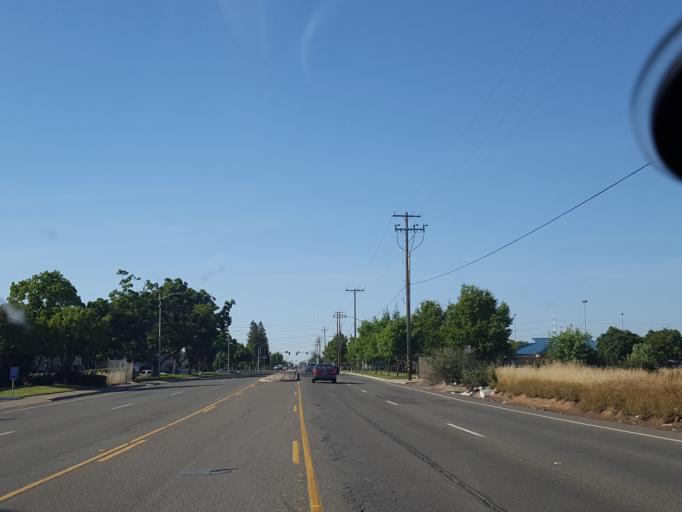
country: US
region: California
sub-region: Sacramento County
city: Florin
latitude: 38.5028
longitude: -121.3906
